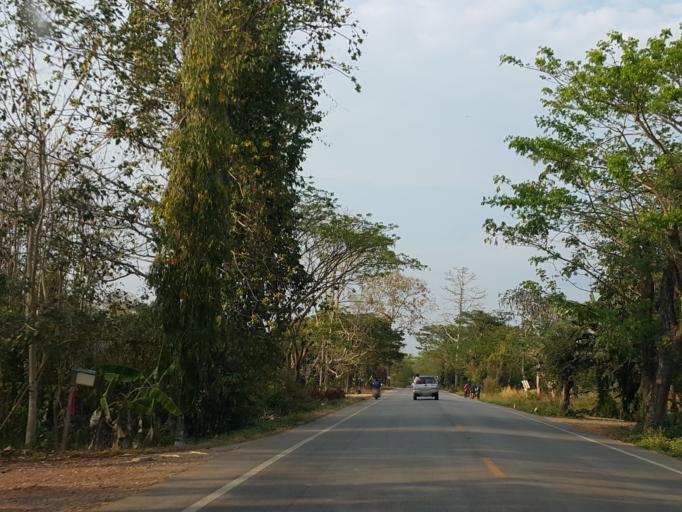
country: TH
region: Lampang
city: Chae Hom
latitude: 18.5156
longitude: 99.4760
